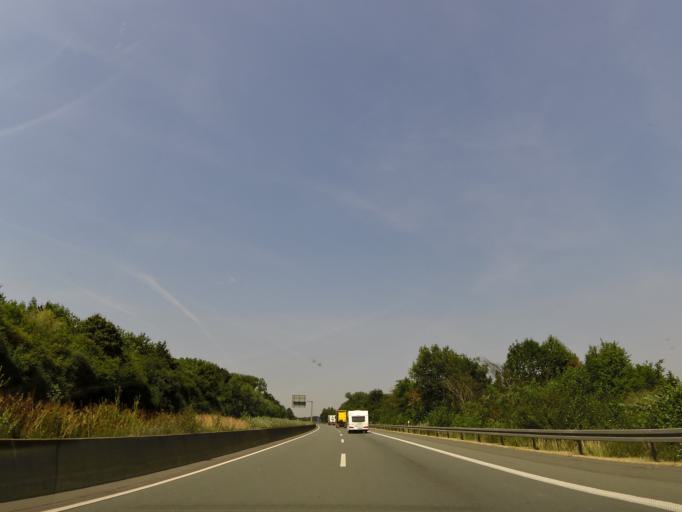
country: DE
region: North Rhine-Westphalia
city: Tuernich
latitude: 50.8460
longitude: 6.7463
